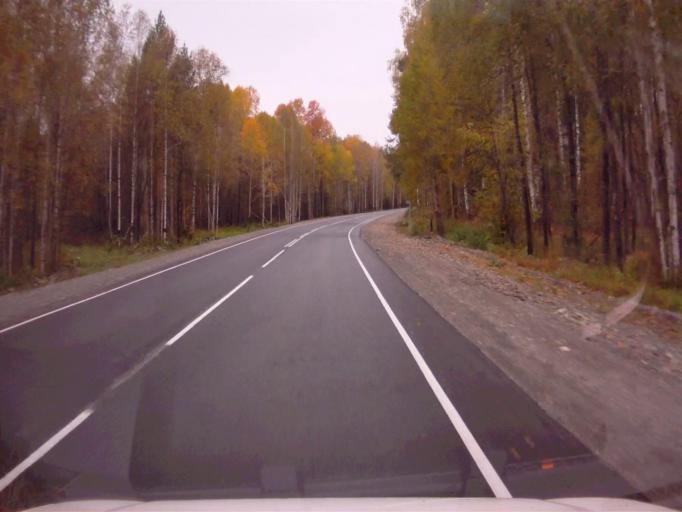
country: RU
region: Chelyabinsk
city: Nyazepetrovsk
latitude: 56.0657
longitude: 59.7012
